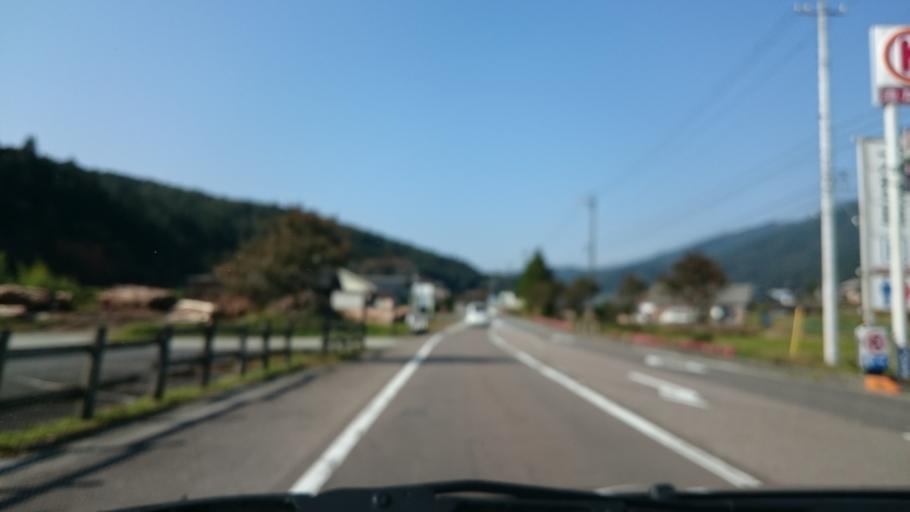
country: JP
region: Gifu
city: Nakatsugawa
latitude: 35.7006
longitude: 137.3798
